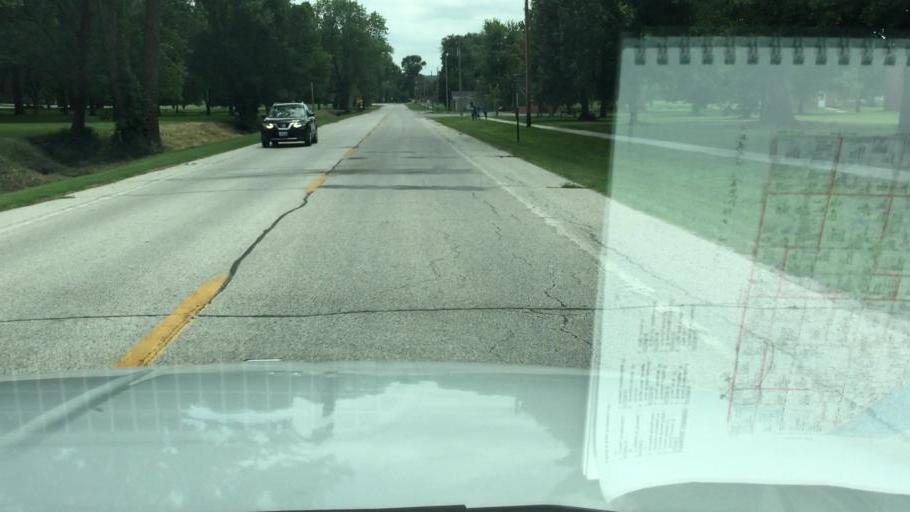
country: US
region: Illinois
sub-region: Hancock County
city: Nauvoo
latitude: 40.5452
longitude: -91.3866
